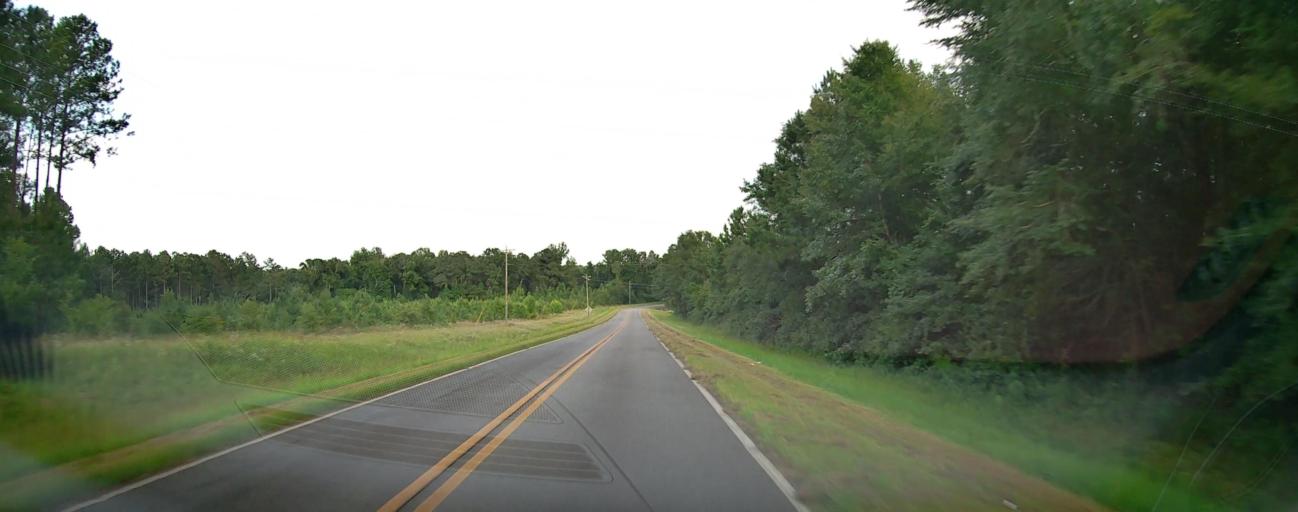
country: US
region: Georgia
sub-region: Crawford County
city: Roberta
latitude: 32.6703
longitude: -84.0720
